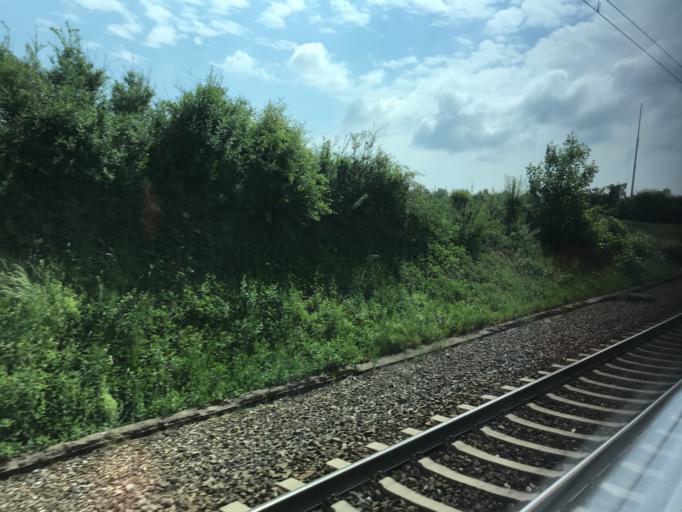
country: DE
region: Baden-Wuerttemberg
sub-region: Tuebingen Region
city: Beimerstetten
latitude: 48.4558
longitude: 9.9759
